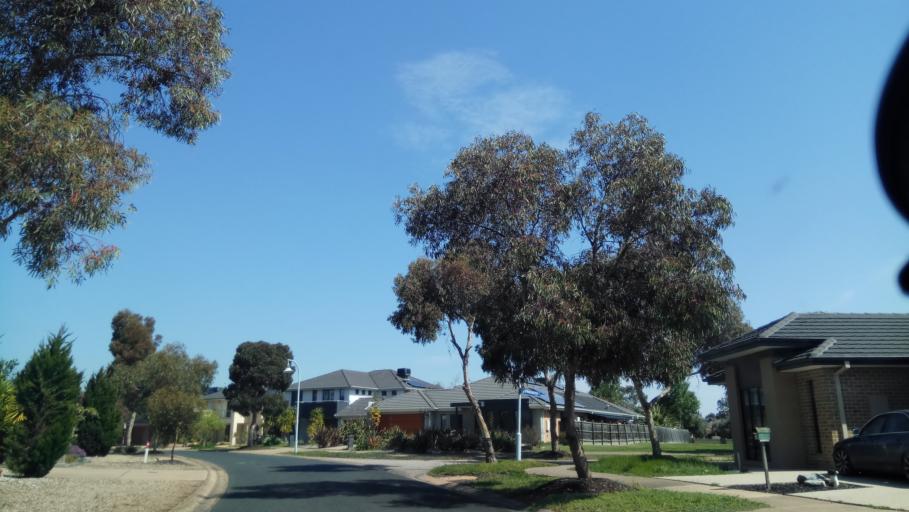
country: AU
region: Victoria
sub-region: Hobsons Bay
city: Altona Meadows
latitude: -37.8879
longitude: 144.7718
